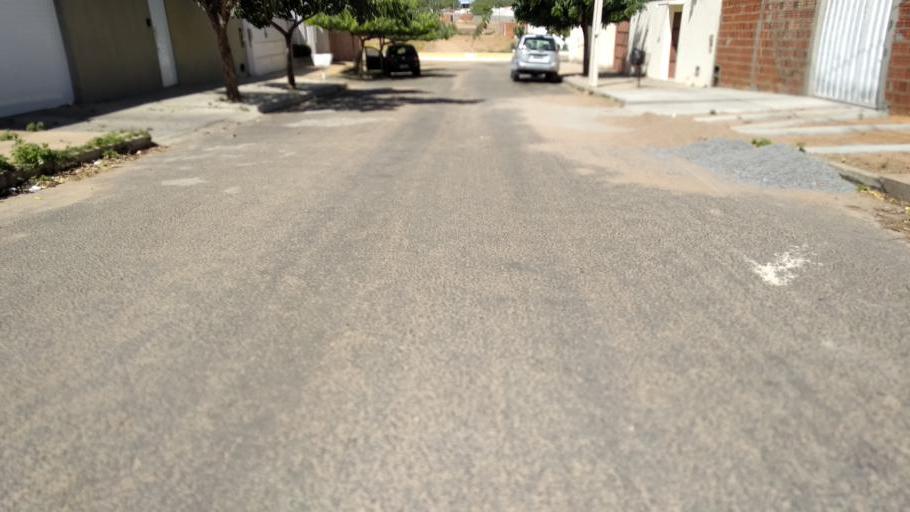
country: BR
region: Bahia
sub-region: Guanambi
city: Guanambi
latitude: -14.2293
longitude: -42.7739
